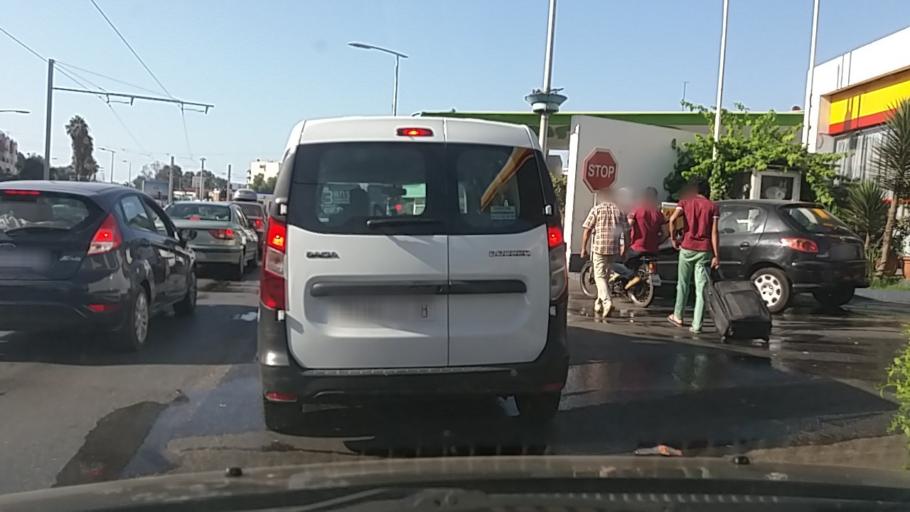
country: MA
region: Rabat-Sale-Zemmour-Zaer
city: Sale
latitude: 34.0396
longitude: -6.8158
